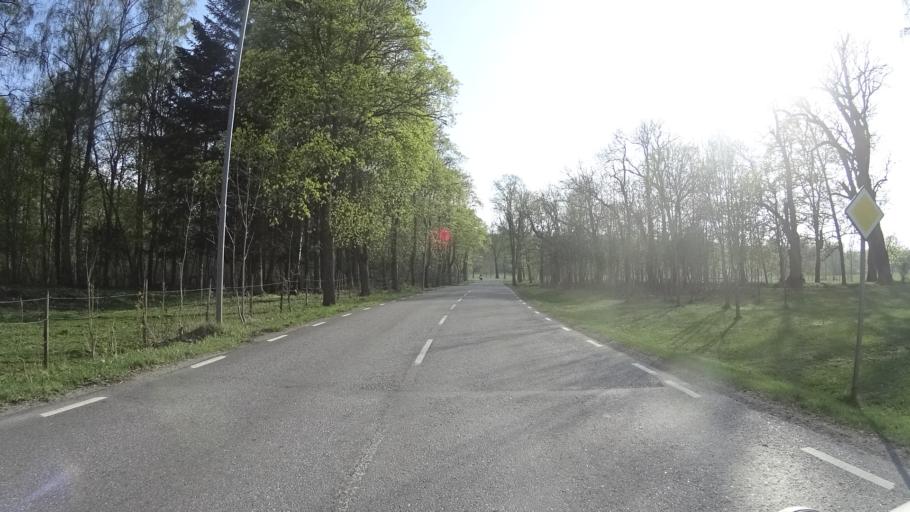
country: SE
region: Vaestra Goetaland
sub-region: Gotene Kommun
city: Goetene
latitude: 58.6242
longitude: 13.4259
